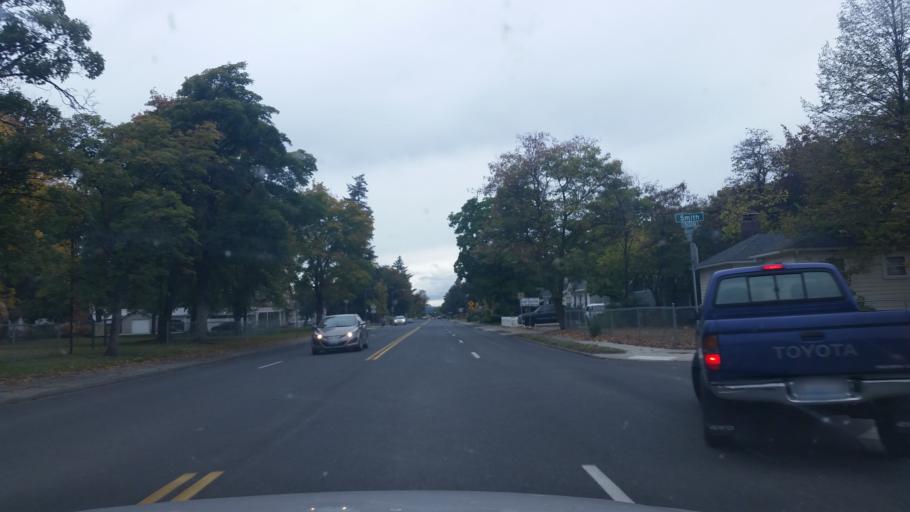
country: US
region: Washington
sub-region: Spokane County
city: Spokane
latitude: 47.6719
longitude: -117.3723
